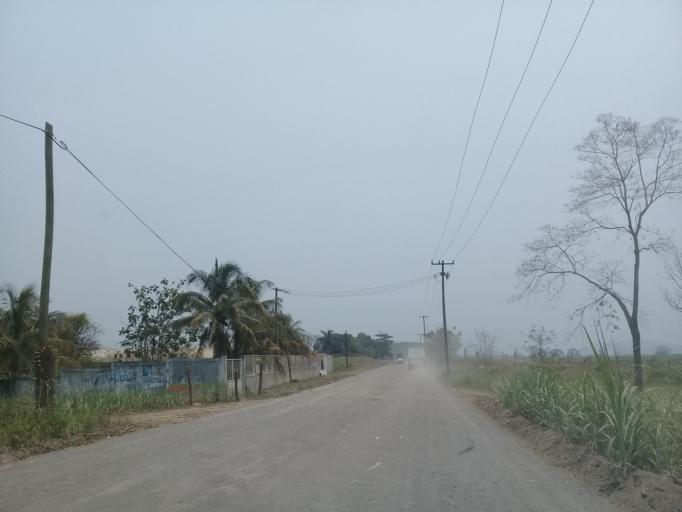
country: MX
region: Veracruz
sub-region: Tezonapa
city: Laguna Chica (Pueblo Nuevo)
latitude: 18.5381
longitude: -96.7390
